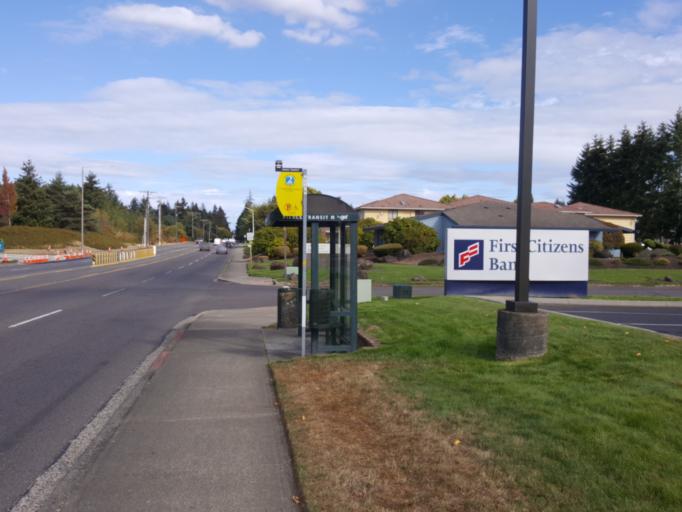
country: US
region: Washington
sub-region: Pierce County
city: Fircrest
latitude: 47.2427
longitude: -122.5231
